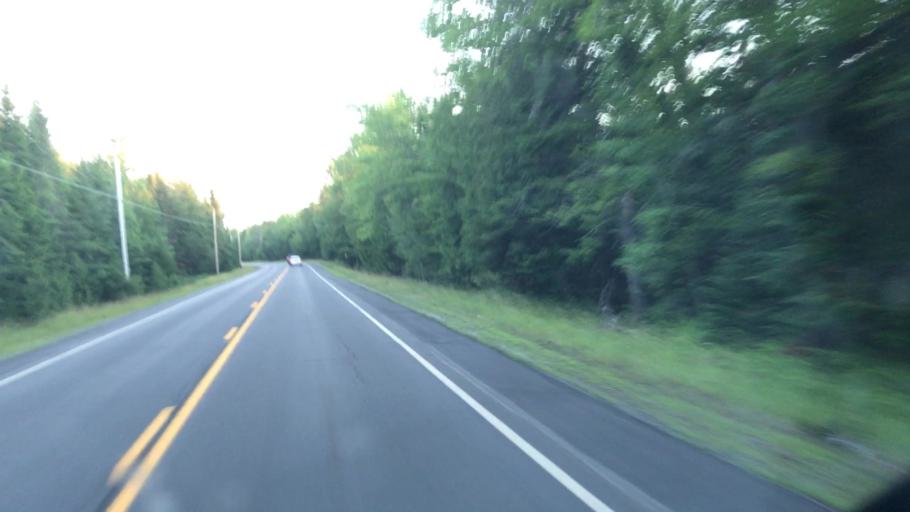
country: US
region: Maine
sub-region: Penobscot County
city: Medway
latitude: 45.5789
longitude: -68.3186
